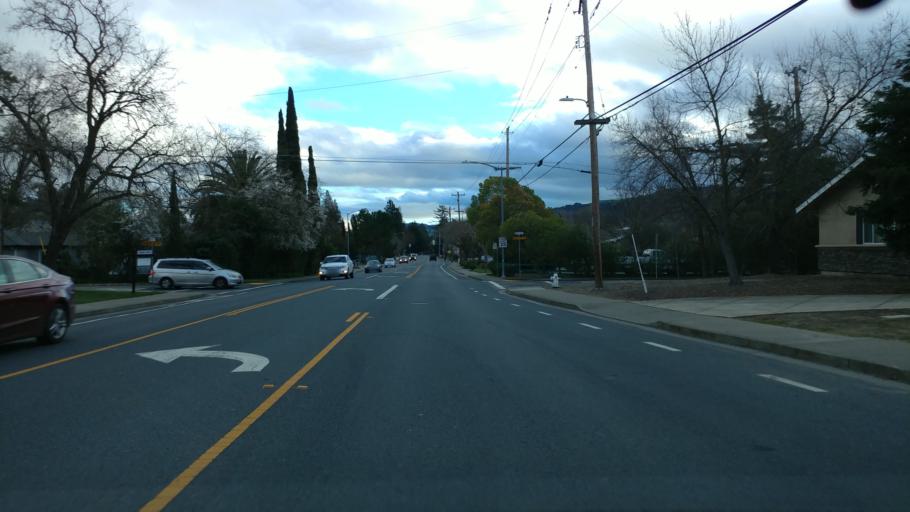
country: US
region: California
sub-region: Contra Costa County
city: Danville
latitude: 37.8294
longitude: -121.9873
